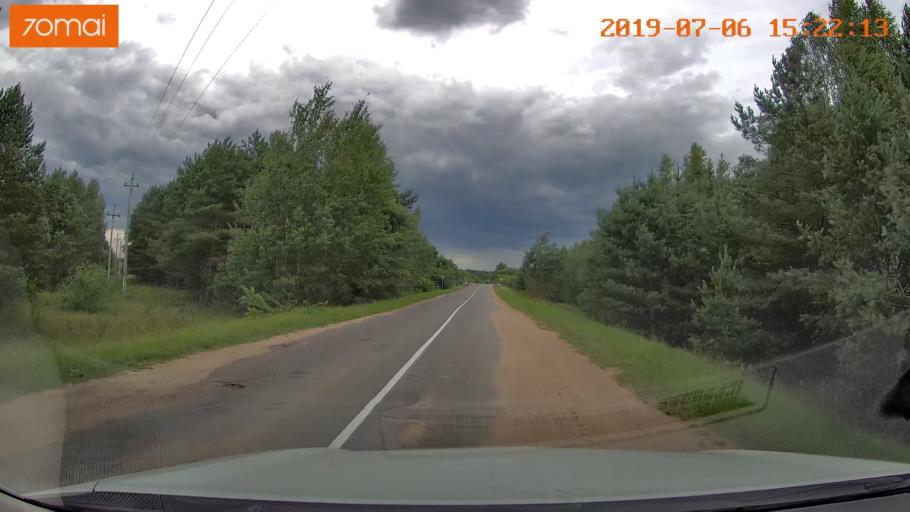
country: BY
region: Minsk
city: Valozhyn
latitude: 54.0118
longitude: 26.6063
